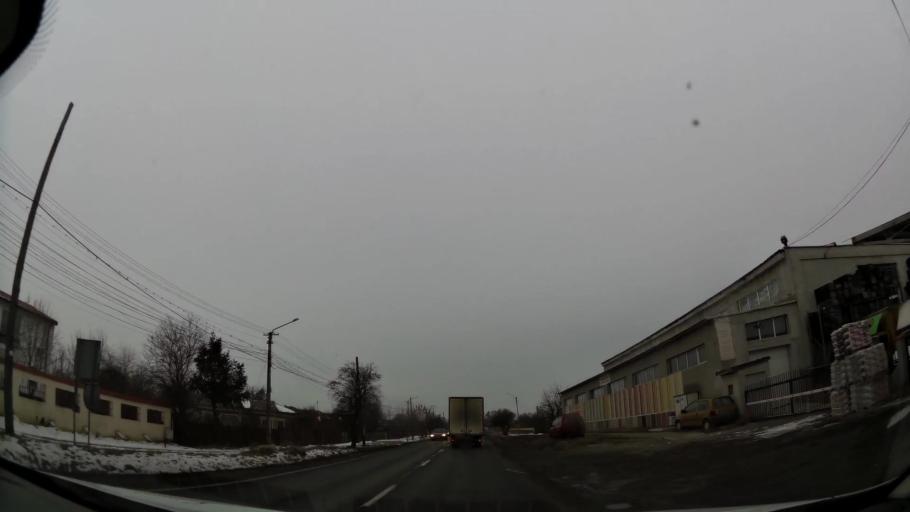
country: RO
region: Dambovita
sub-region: Comuna Racari
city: Racari
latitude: 44.6209
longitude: 25.7532
